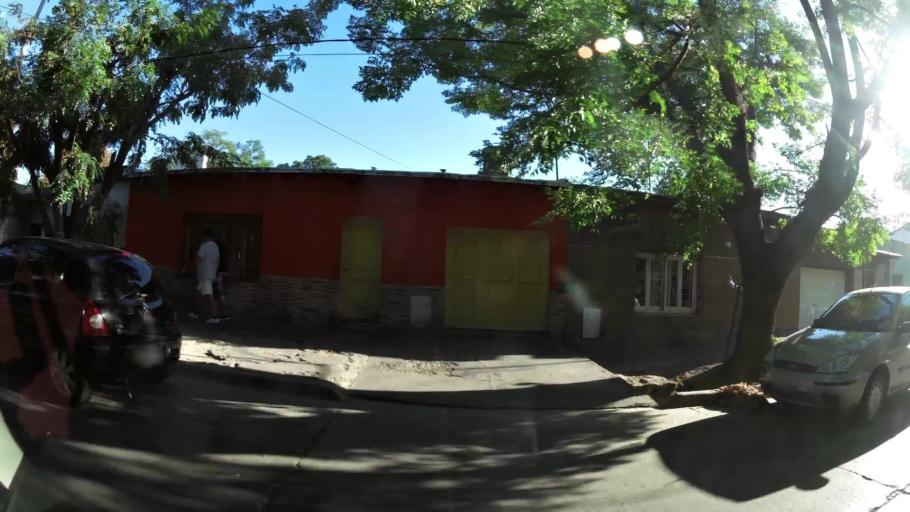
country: AR
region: Mendoza
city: Las Heras
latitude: -32.8671
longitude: -68.8194
